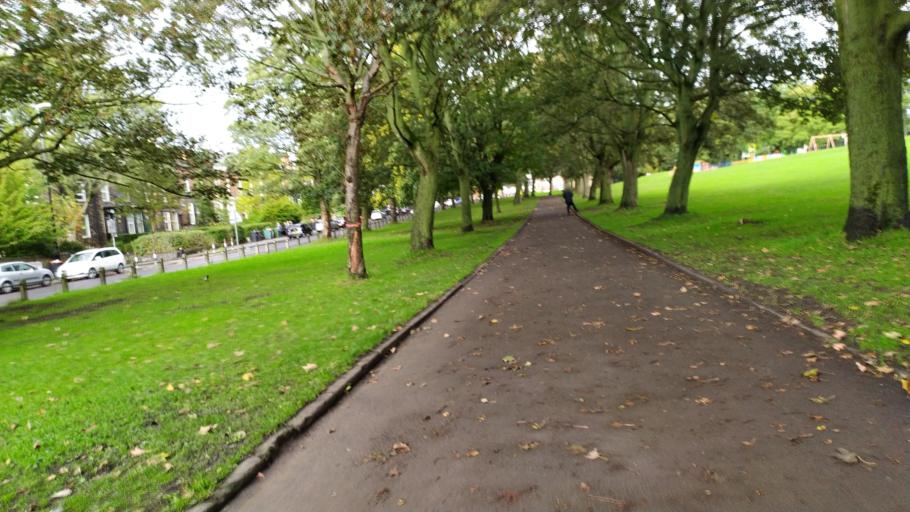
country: GB
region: England
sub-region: City and Borough of Leeds
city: Leeds
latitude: 53.8124
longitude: -1.5635
